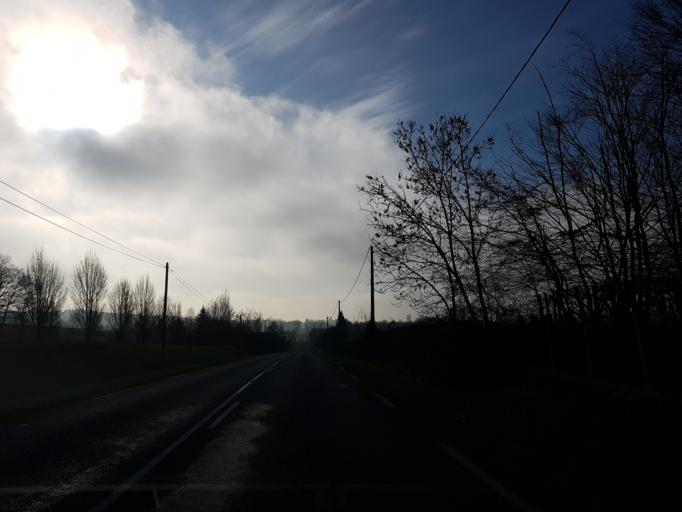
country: FR
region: Bourgogne
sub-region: Departement de Saone-et-Loire
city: Gueugnon
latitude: 46.6209
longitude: 4.0824
